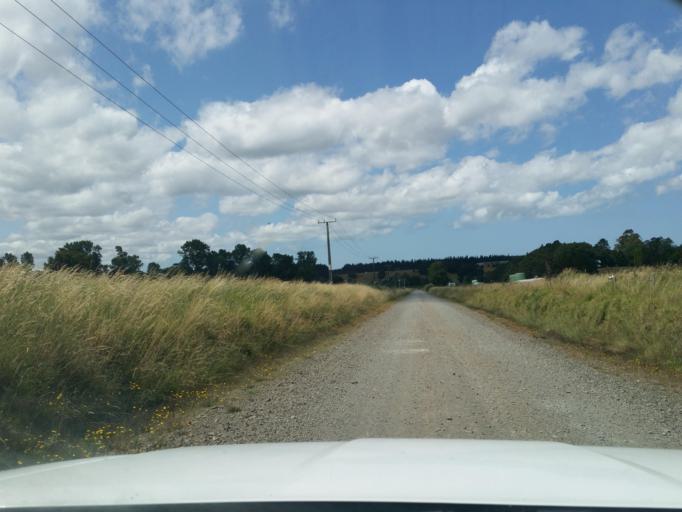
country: NZ
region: Northland
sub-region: Kaipara District
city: Dargaville
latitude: -35.8018
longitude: 173.7313
